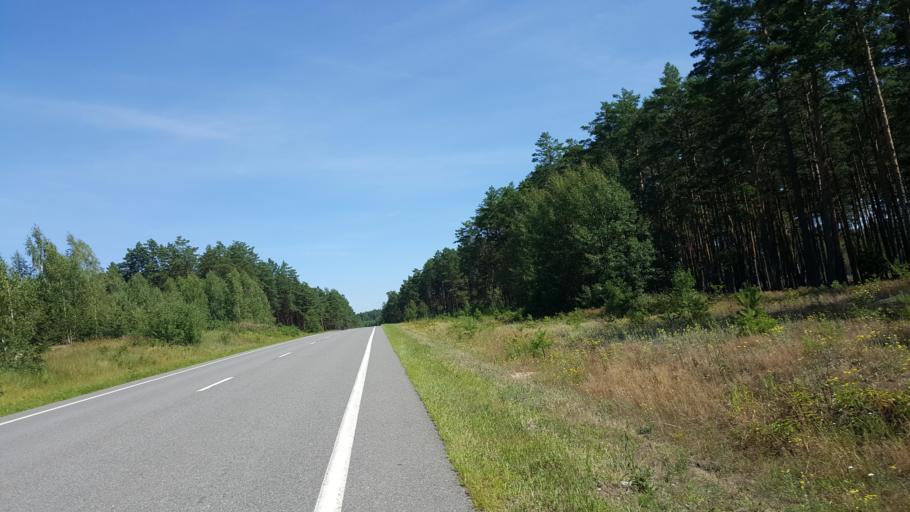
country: BY
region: Brest
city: Zhabinka
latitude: 52.4406
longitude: 24.1312
